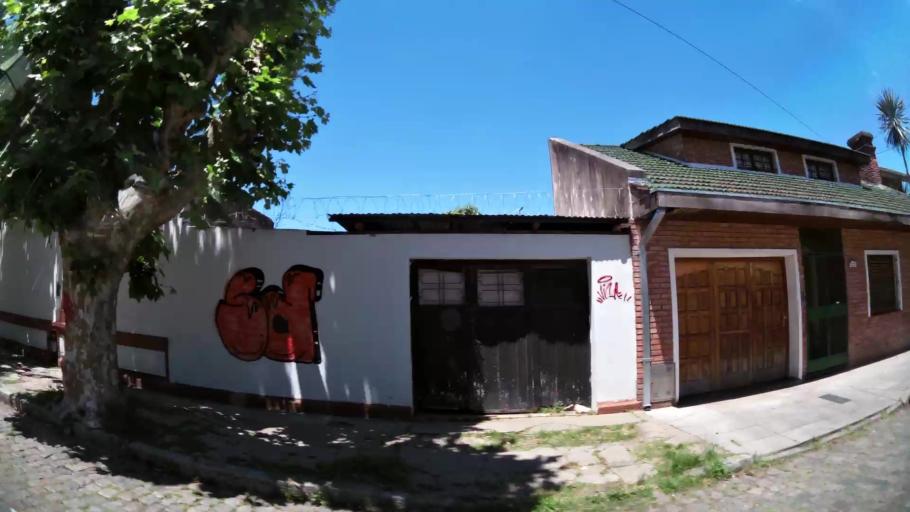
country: AR
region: Buenos Aires
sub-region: Partido de Tigre
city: Tigre
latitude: -34.4458
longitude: -58.5529
